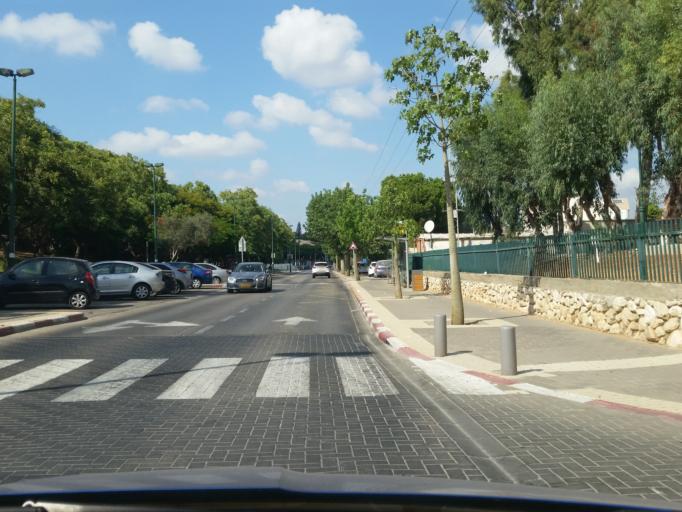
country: IL
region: Tel Aviv
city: Ramat HaSharon
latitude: 32.1170
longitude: 34.8338
